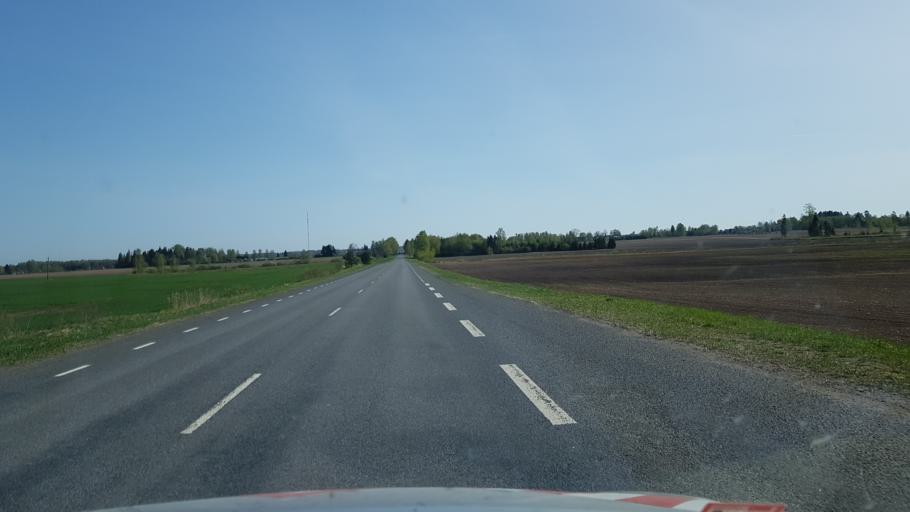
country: EE
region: Viljandimaa
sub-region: Karksi vald
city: Karksi-Nuia
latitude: 58.1785
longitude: 25.4942
